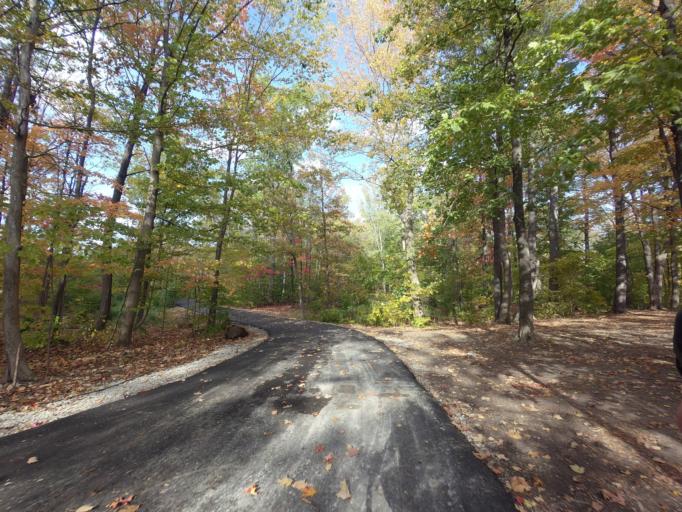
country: CA
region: Ontario
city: Mississauga
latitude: 43.5402
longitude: -79.6871
